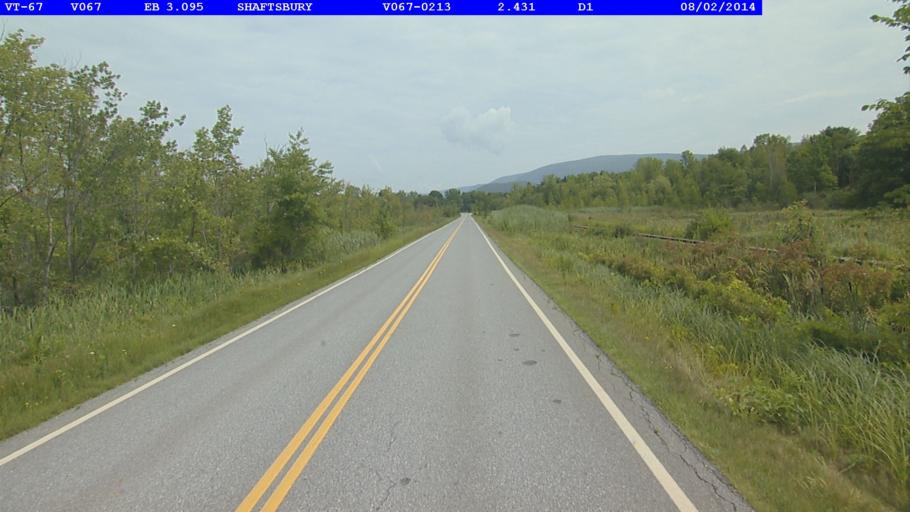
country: US
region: Vermont
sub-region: Bennington County
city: North Bennington
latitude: 42.9398
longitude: -73.2289
